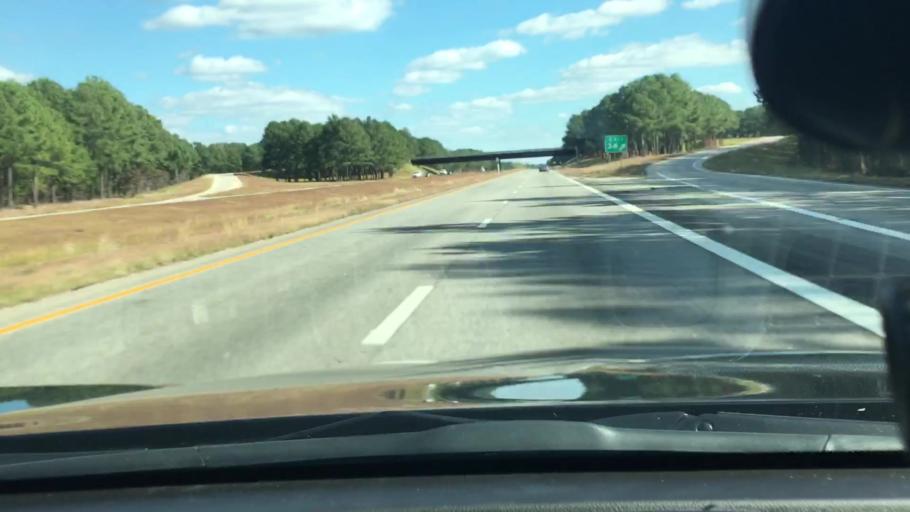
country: US
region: North Carolina
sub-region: Wilson County
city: Lucama
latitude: 35.7750
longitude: -78.0616
